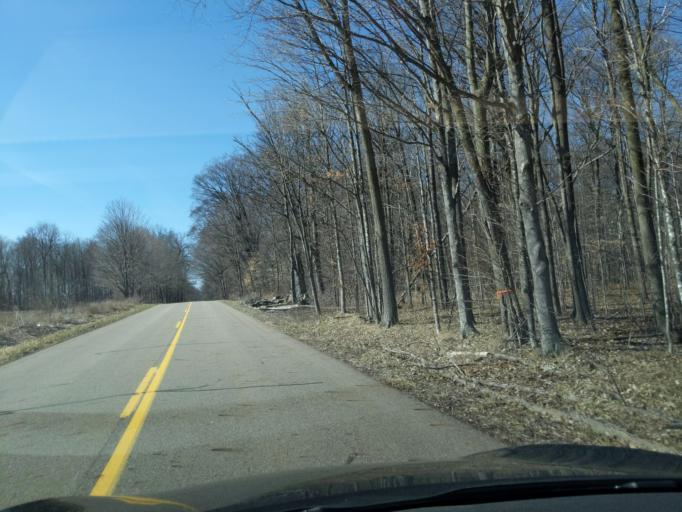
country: US
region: Michigan
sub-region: Ionia County
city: Lake Odessa
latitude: 42.7270
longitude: -85.0402
